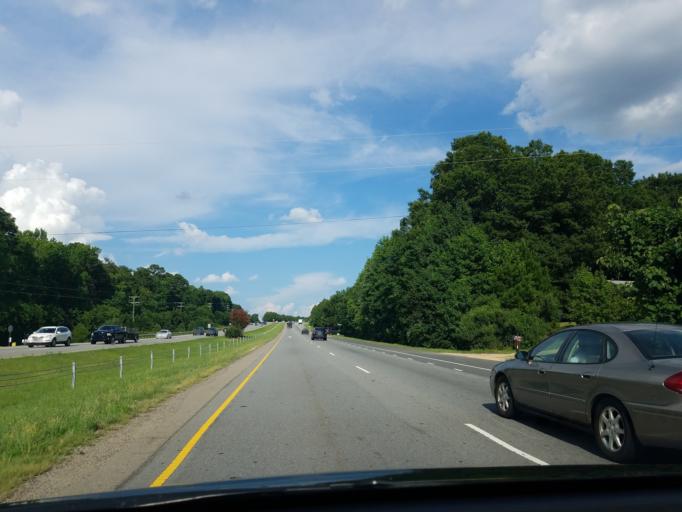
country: US
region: North Carolina
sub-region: Wake County
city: Apex
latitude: 35.7495
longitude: -78.8597
